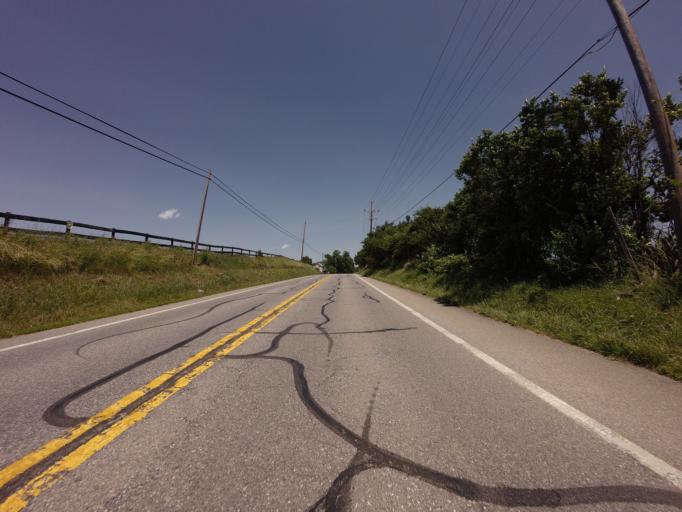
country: US
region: Maryland
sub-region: Frederick County
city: Brunswick
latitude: 39.3497
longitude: -77.6019
